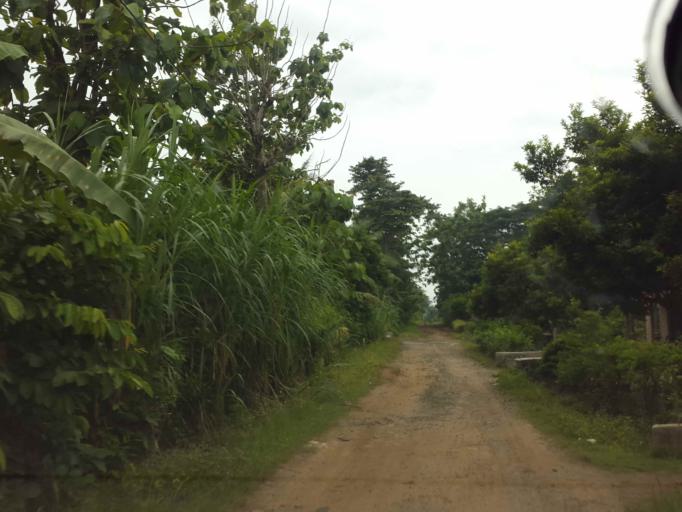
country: ID
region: Lampung
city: Sidorejo
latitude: -5.6057
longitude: 105.5337
